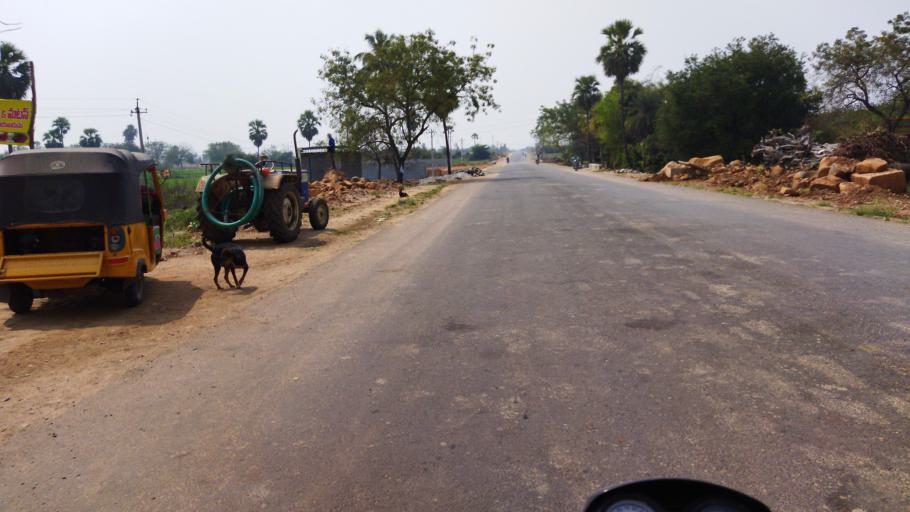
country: IN
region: Telangana
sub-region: Nalgonda
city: Nalgonda
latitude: 17.1510
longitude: 79.4047
